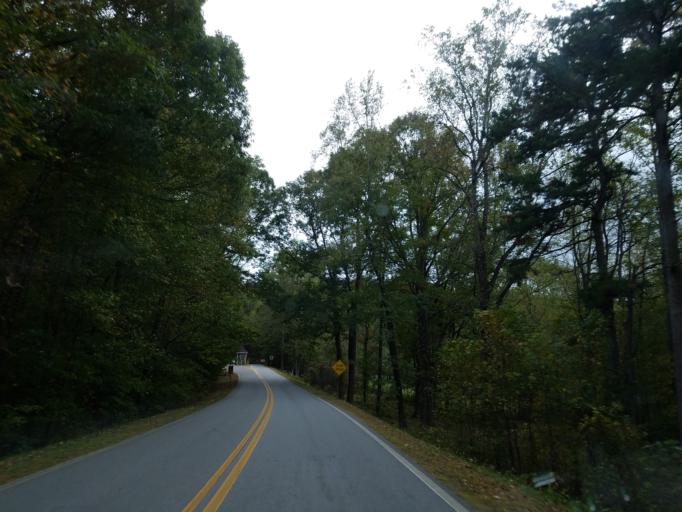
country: US
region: Georgia
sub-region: Dawson County
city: Dawsonville
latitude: 34.5562
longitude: -84.2507
